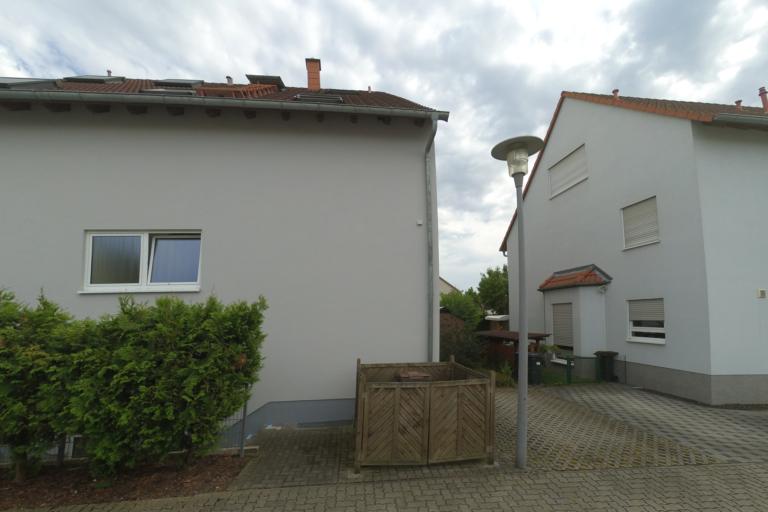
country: DE
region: Rheinland-Pfalz
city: Altrip
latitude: 49.4346
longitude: 8.4900
